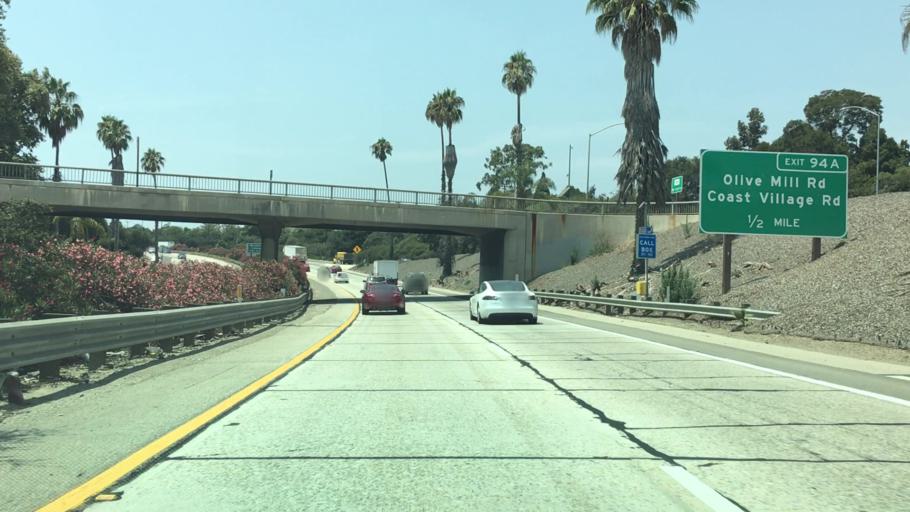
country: US
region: California
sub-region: Santa Barbara County
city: Montecito
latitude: 34.4223
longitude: -119.6309
